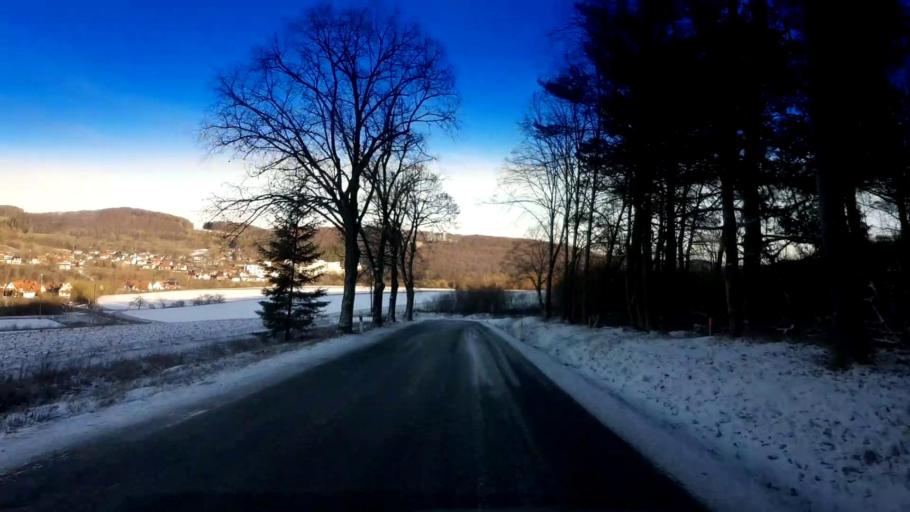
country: DE
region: Bavaria
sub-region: Upper Franconia
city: Heiligenstadt
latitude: 49.8593
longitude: 11.1586
